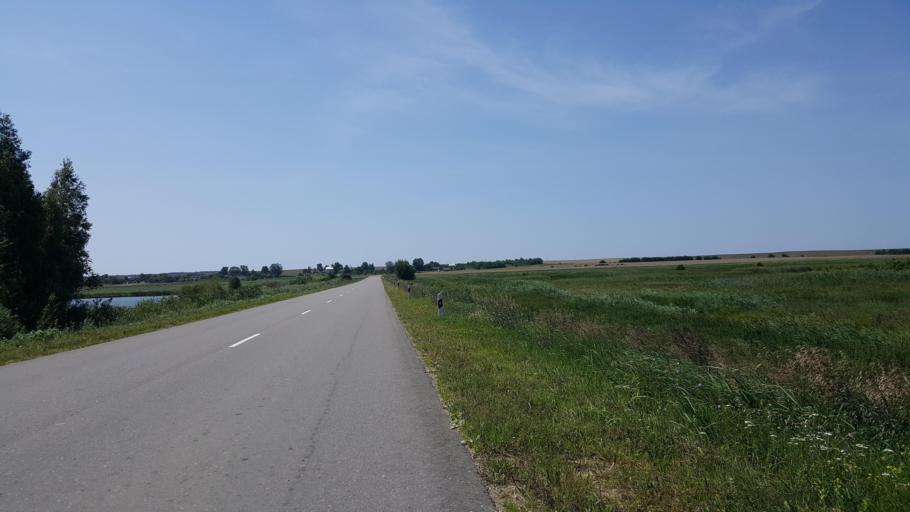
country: BY
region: Brest
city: Vysokaye
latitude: 52.3634
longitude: 23.5177
